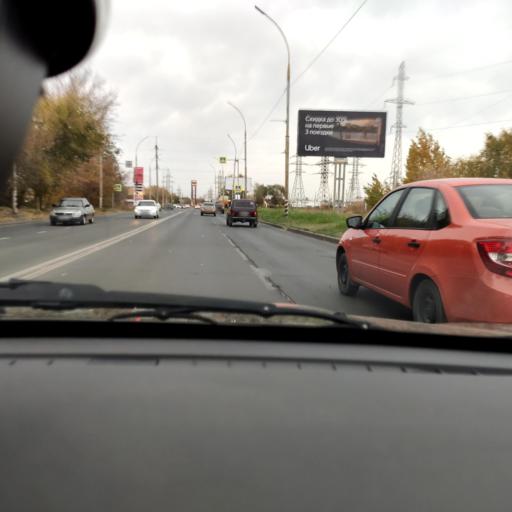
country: RU
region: Samara
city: Tol'yatti
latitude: 53.5478
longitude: 49.3172
